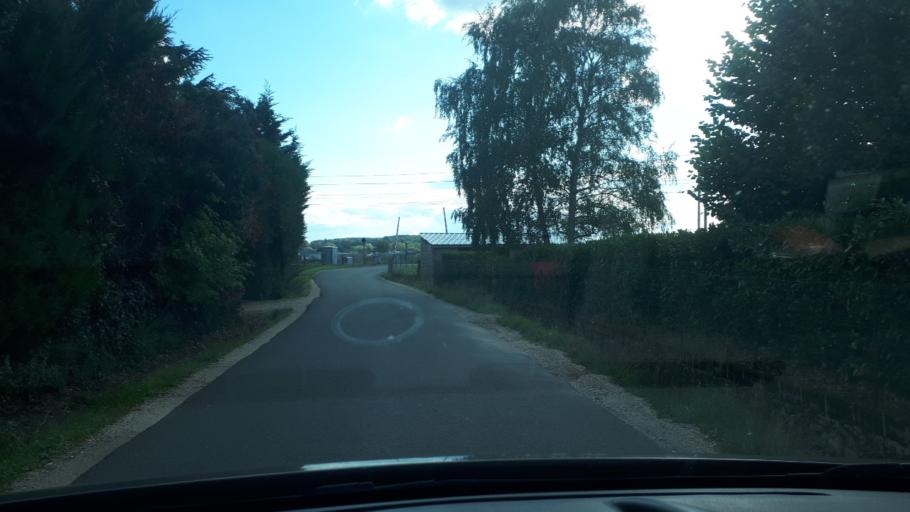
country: FR
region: Centre
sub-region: Departement du Loir-et-Cher
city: Saint-Aignan
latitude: 47.2910
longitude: 1.3766
